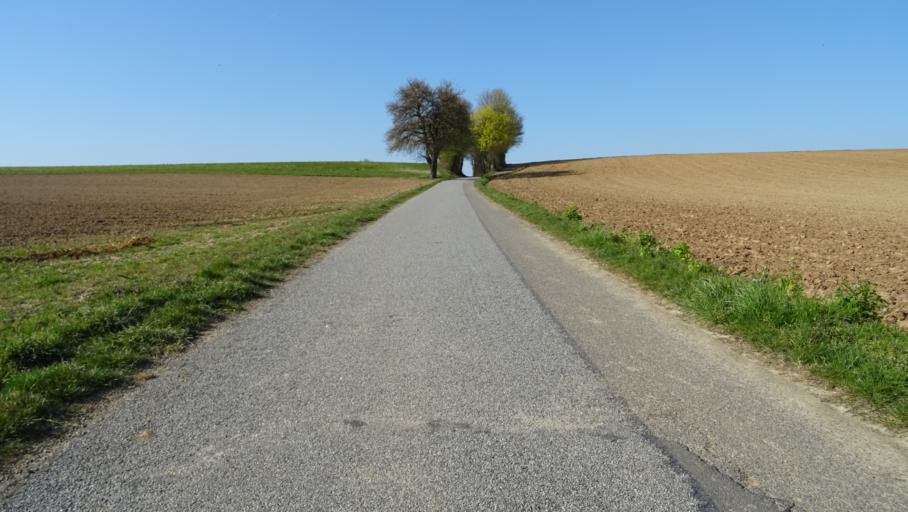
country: DE
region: Baden-Wuerttemberg
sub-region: Karlsruhe Region
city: Billigheim
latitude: 49.3786
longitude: 9.2296
